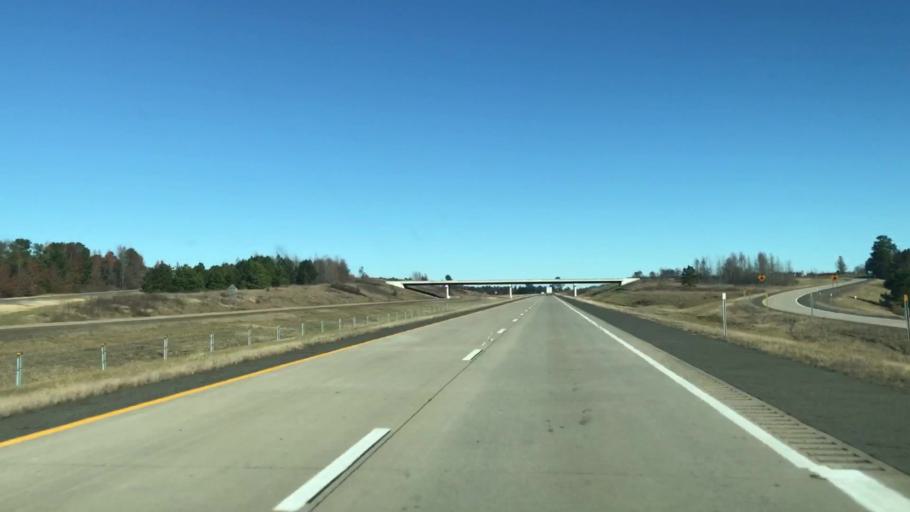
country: US
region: Texas
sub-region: Cass County
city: Queen City
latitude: 33.1167
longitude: -93.8937
